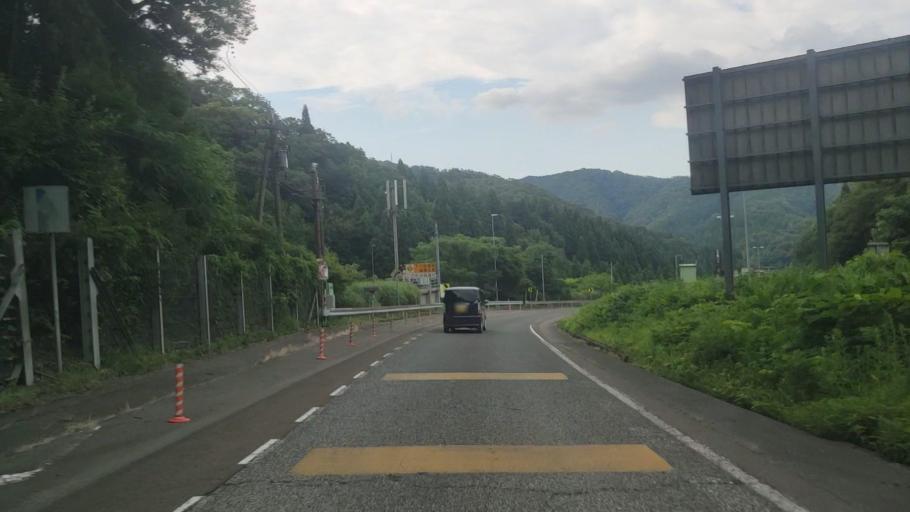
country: JP
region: Fukui
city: Takefu
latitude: 35.8490
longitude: 136.1257
